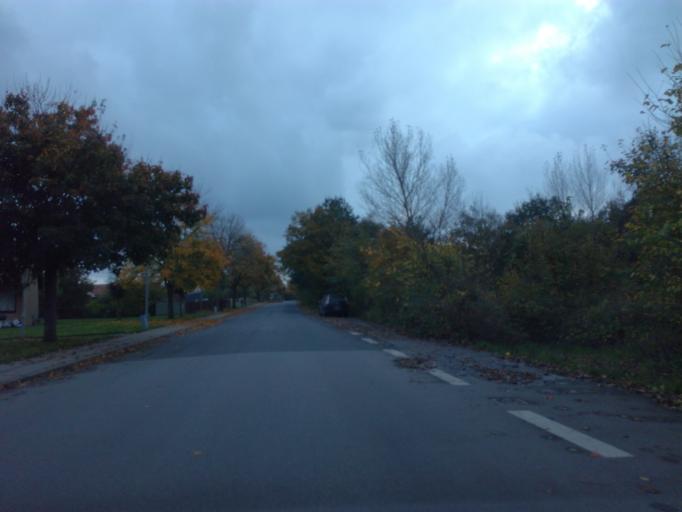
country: DK
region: South Denmark
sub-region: Vejle Kommune
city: Borkop
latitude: 55.6429
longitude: 9.6564
